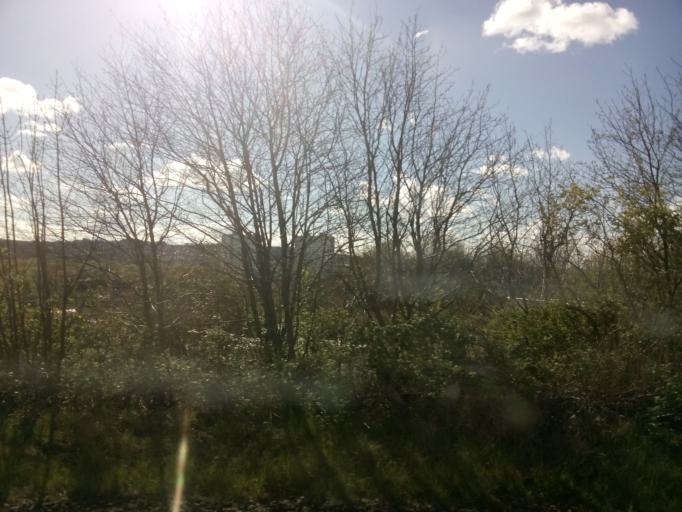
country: GB
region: England
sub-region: Gateshead
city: Gateshead
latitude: 54.9527
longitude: -1.6196
